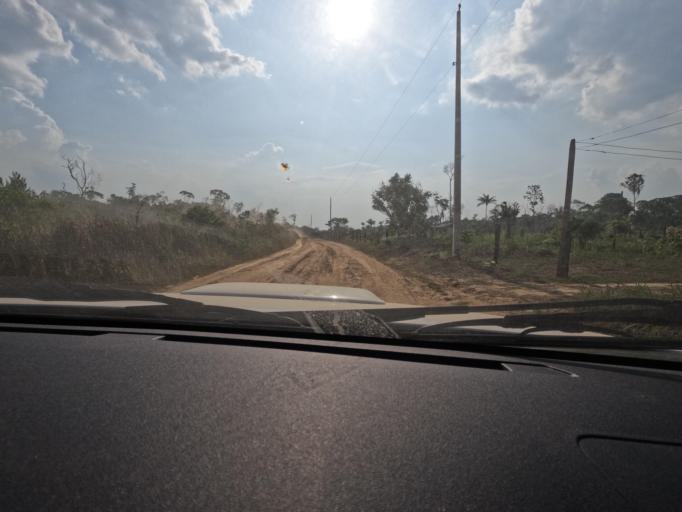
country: BR
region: Rondonia
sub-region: Porto Velho
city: Porto Velho
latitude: -8.5743
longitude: -63.9994
